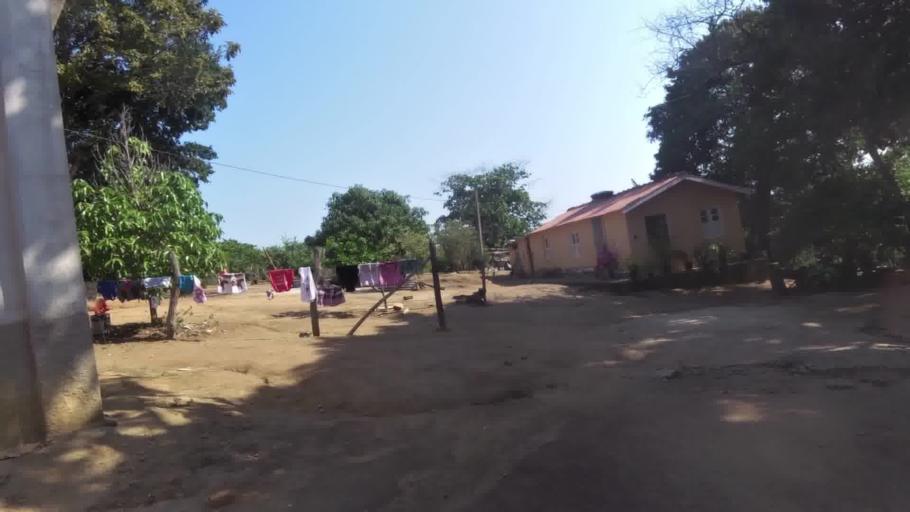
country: BR
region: Espirito Santo
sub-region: Piuma
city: Piuma
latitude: -20.8121
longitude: -40.7374
